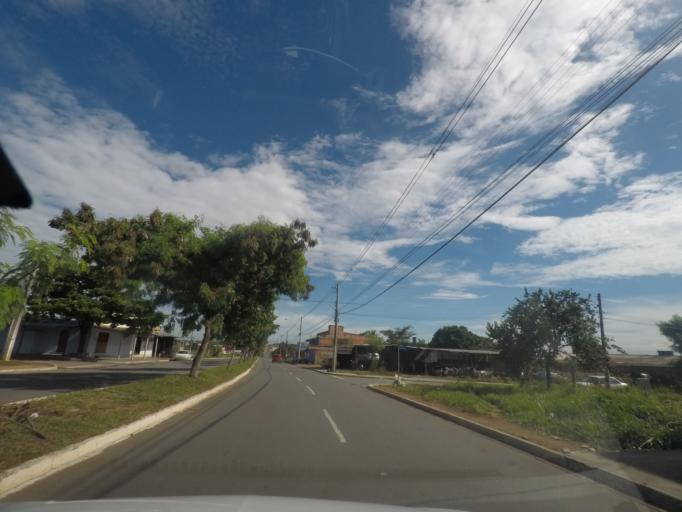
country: BR
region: Goias
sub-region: Aparecida De Goiania
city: Aparecida de Goiania
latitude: -16.8219
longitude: -49.2782
